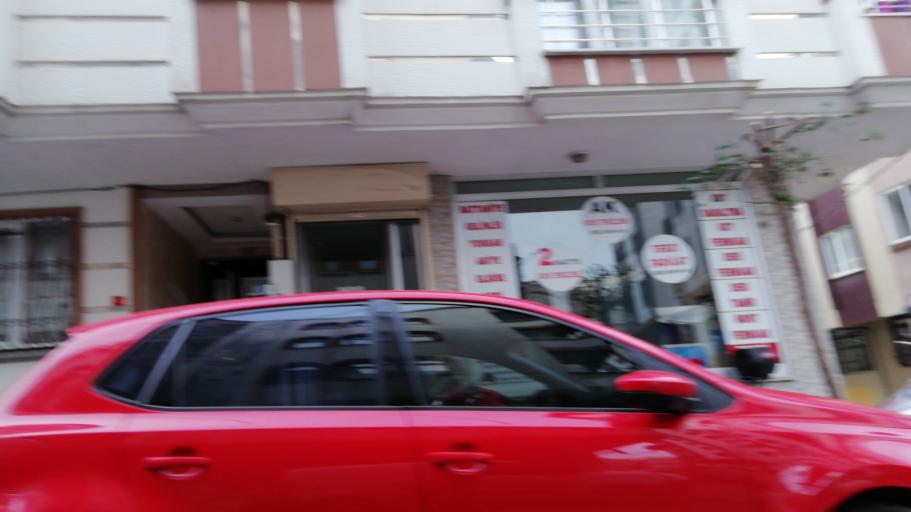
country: TR
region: Istanbul
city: Bagcilar
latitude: 41.0240
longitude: 28.8344
